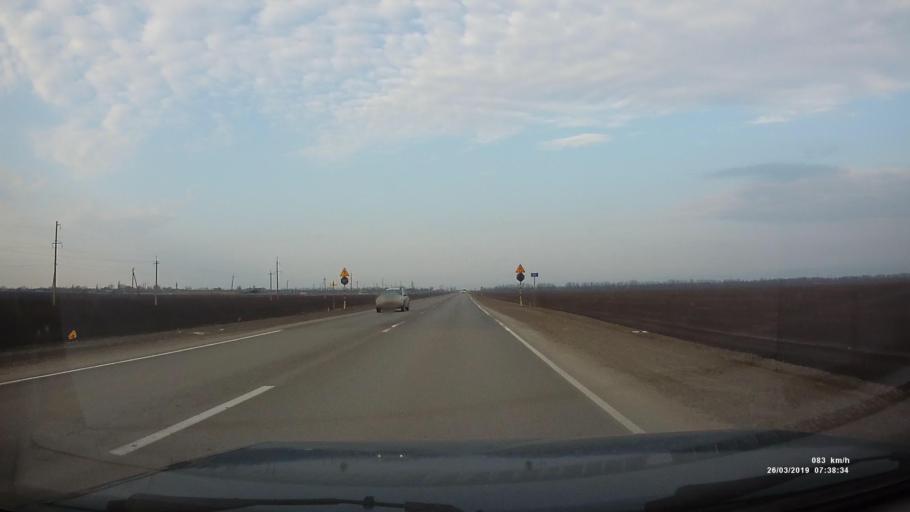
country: RU
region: Rostov
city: Novobessergenovka
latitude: 47.1994
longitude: 38.6813
